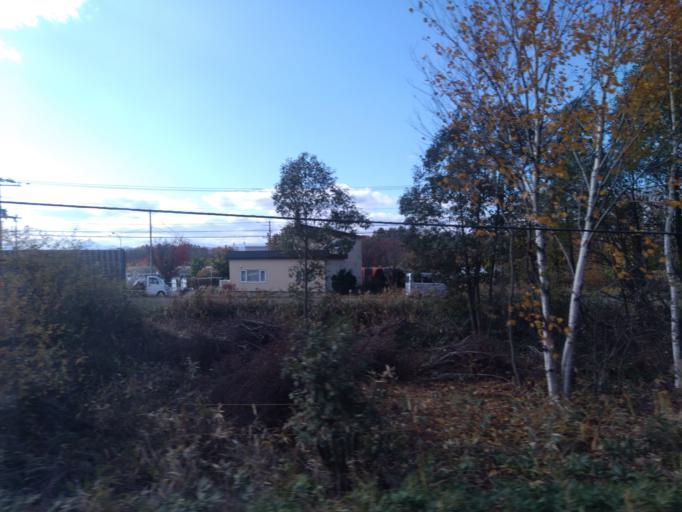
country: JP
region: Hokkaido
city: Kitahiroshima
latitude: 42.9098
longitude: 141.5740
